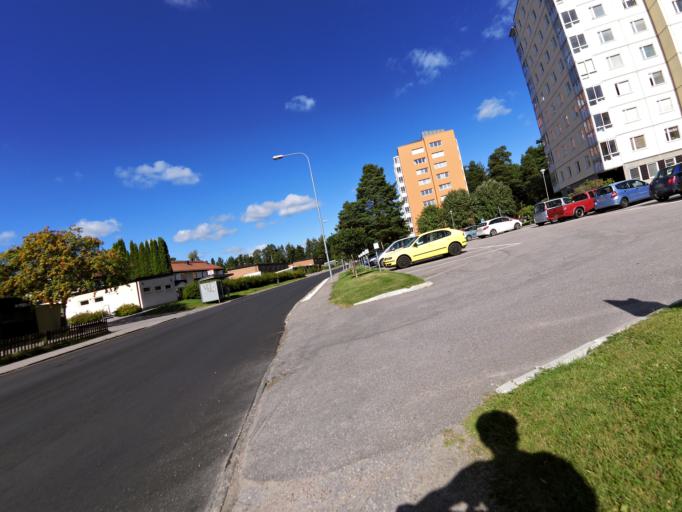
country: SE
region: Gaevleborg
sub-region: Gavle Kommun
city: Gavle
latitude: 60.6967
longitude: 17.1459
